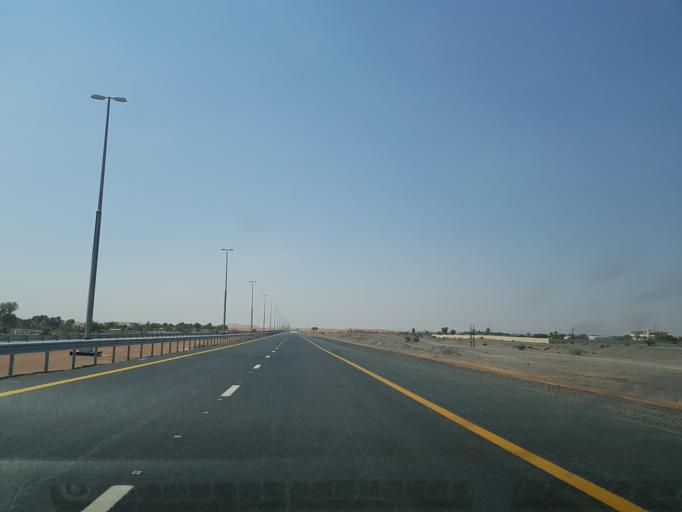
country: AE
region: Ash Shariqah
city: Adh Dhayd
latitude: 25.2360
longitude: 55.9027
